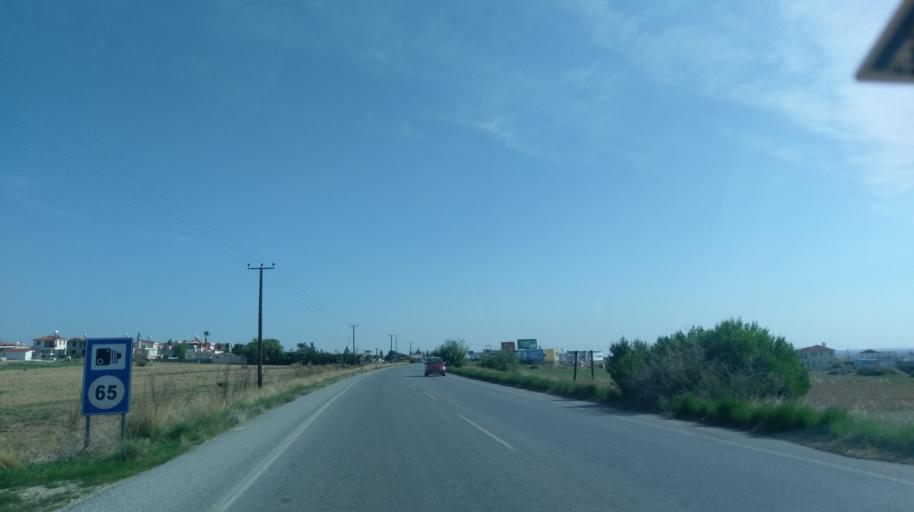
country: CY
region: Ammochostos
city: Lefkonoiko
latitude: 35.2422
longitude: 33.5947
